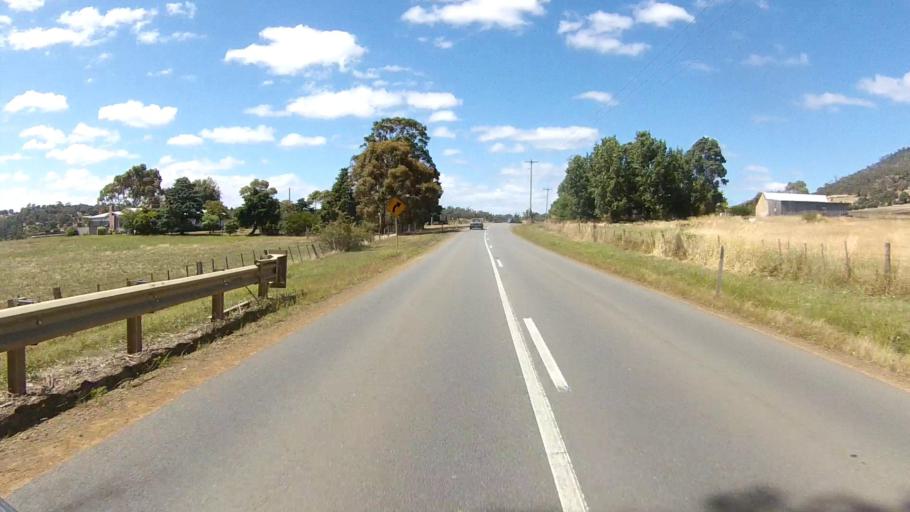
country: AU
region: Tasmania
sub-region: Clarence
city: Cambridge
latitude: -42.8130
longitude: 147.4317
